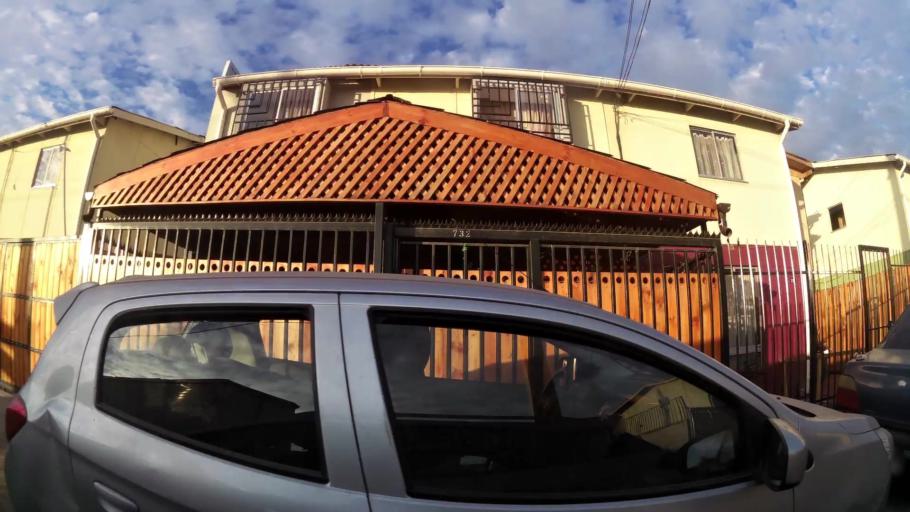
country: CL
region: Santiago Metropolitan
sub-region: Provincia de Maipo
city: San Bernardo
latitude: -33.6231
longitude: -70.6908
